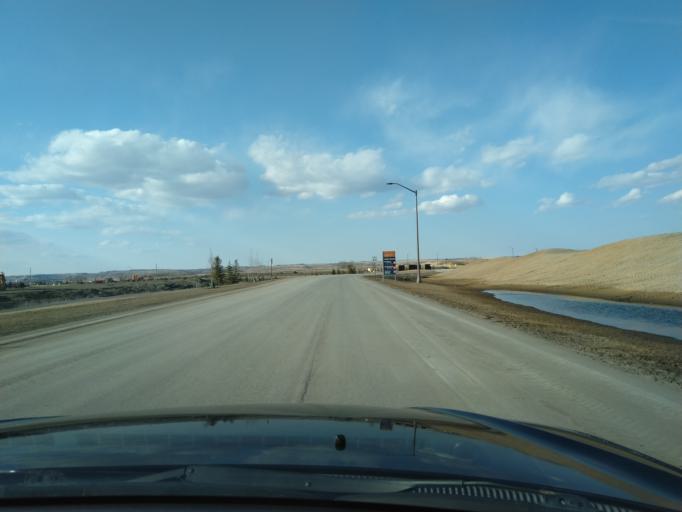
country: CA
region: Alberta
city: Cochrane
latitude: 51.1179
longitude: -114.3889
